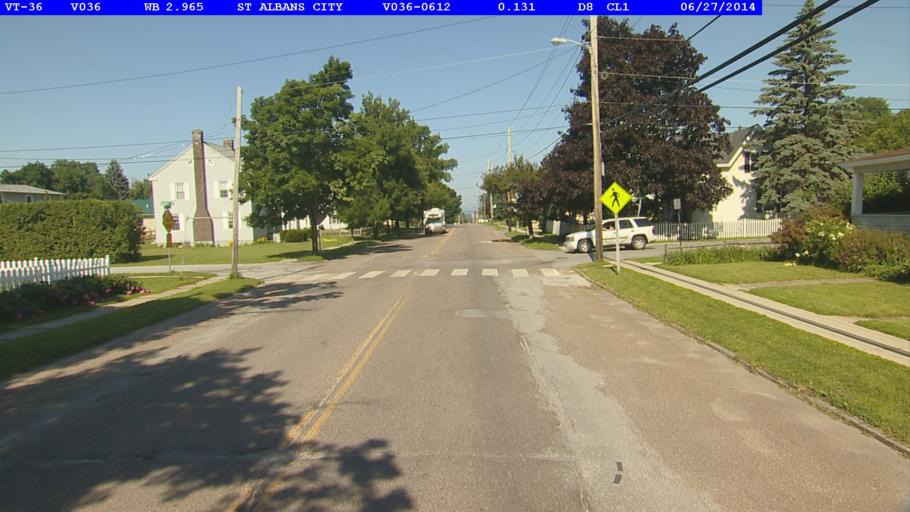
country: US
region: Vermont
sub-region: Franklin County
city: Saint Albans
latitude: 44.8115
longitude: -73.0984
